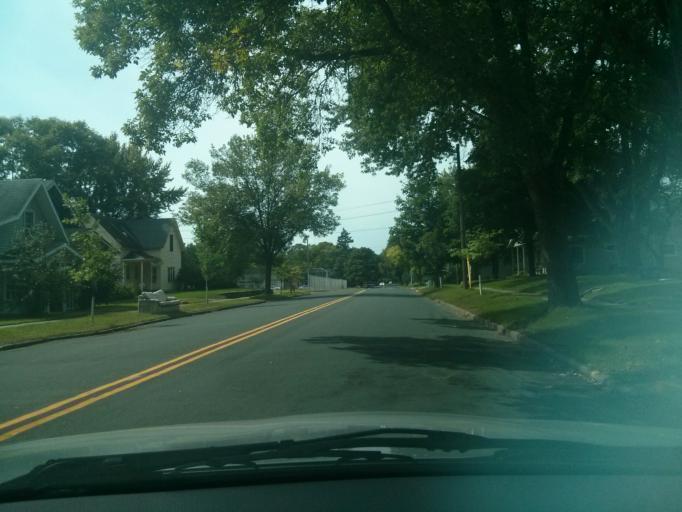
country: US
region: Wisconsin
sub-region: Saint Croix County
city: Hudson
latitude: 44.9822
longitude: -92.7443
